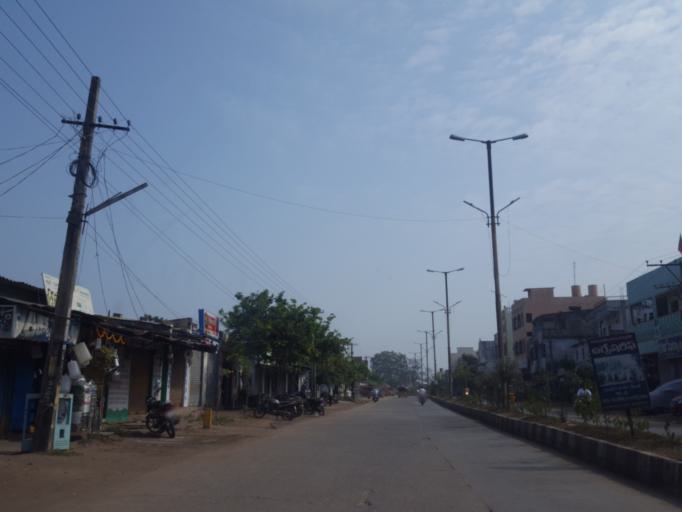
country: IN
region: Telangana
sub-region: Khammam
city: Yellandu
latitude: 17.5930
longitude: 80.3197
